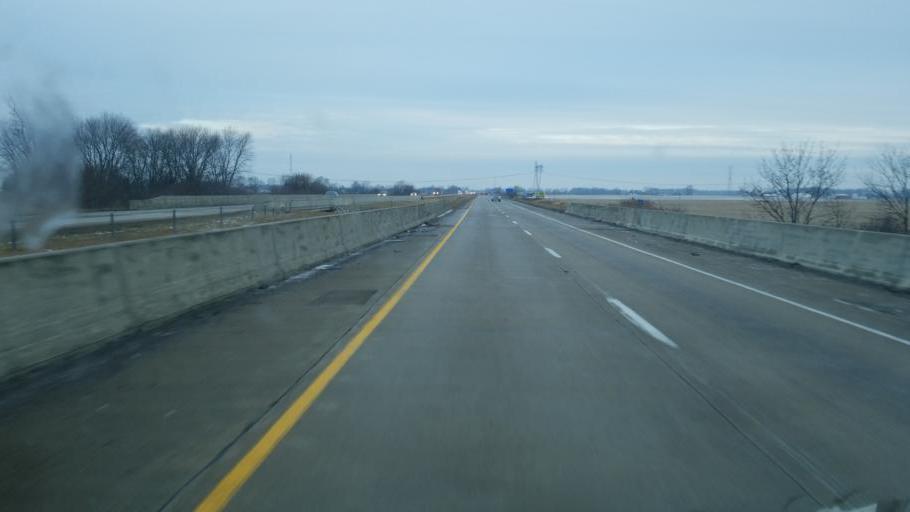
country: US
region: Indiana
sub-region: Hancock County
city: Greenfield
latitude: 39.8259
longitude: -85.6677
